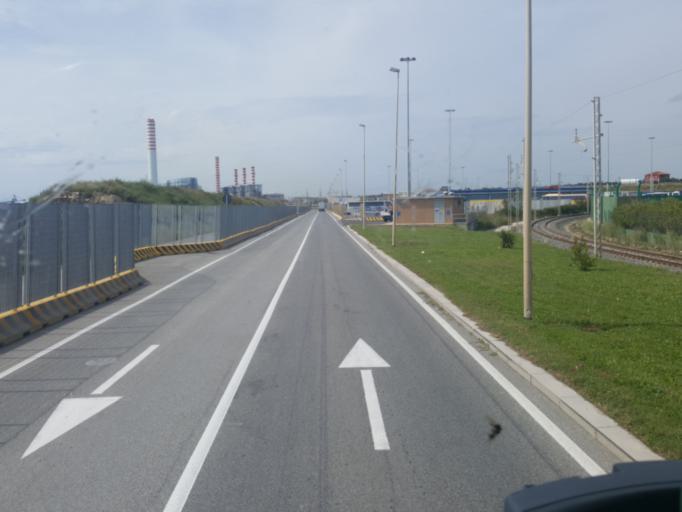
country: IT
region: Latium
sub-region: Citta metropolitana di Roma Capitale
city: Civitavecchia
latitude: 42.1114
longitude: 11.7713
